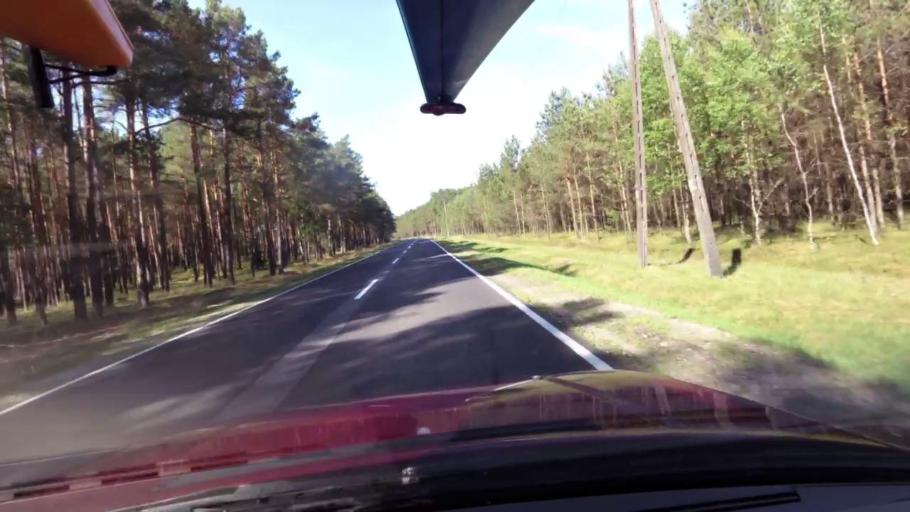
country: PL
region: Pomeranian Voivodeship
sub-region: Powiat bytowski
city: Trzebielino
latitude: 54.1700
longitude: 17.0625
